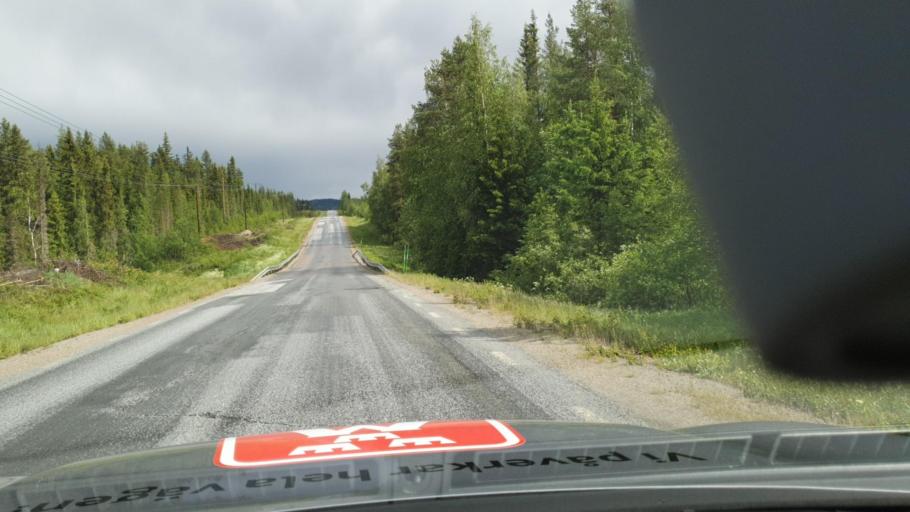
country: SE
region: Vaesternorrland
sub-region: OErnskoeldsviks Kommun
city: Bredbyn
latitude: 63.3724
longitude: 17.9518
